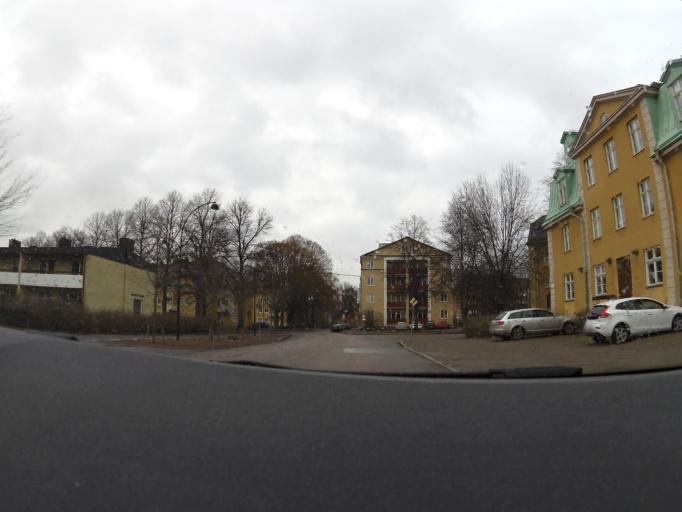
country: SE
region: Gaevleborg
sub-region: Gavle Kommun
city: Gavle
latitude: 60.6690
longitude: 17.1388
